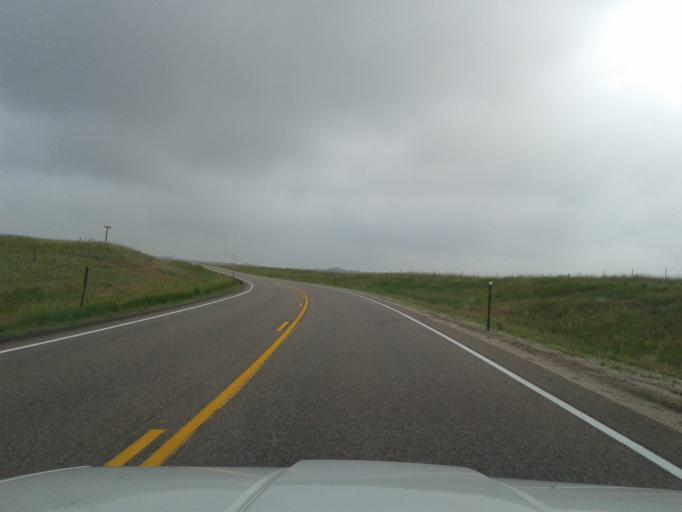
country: US
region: Colorado
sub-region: Elbert County
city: Elizabeth
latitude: 39.2174
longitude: -104.7046
